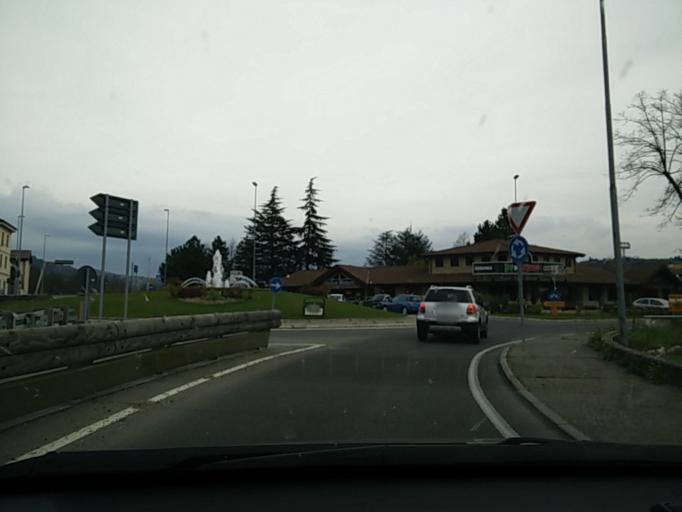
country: IT
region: Lombardy
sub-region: Provincia di Pavia
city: Salice Terme
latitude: 44.9209
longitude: 9.0311
